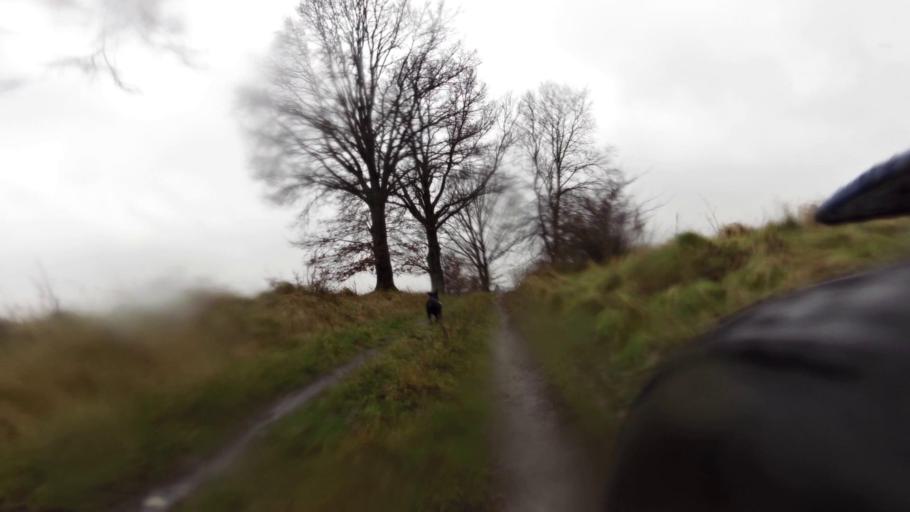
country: PL
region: West Pomeranian Voivodeship
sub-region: Powiat drawski
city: Drawsko Pomorskie
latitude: 53.5526
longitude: 15.8324
